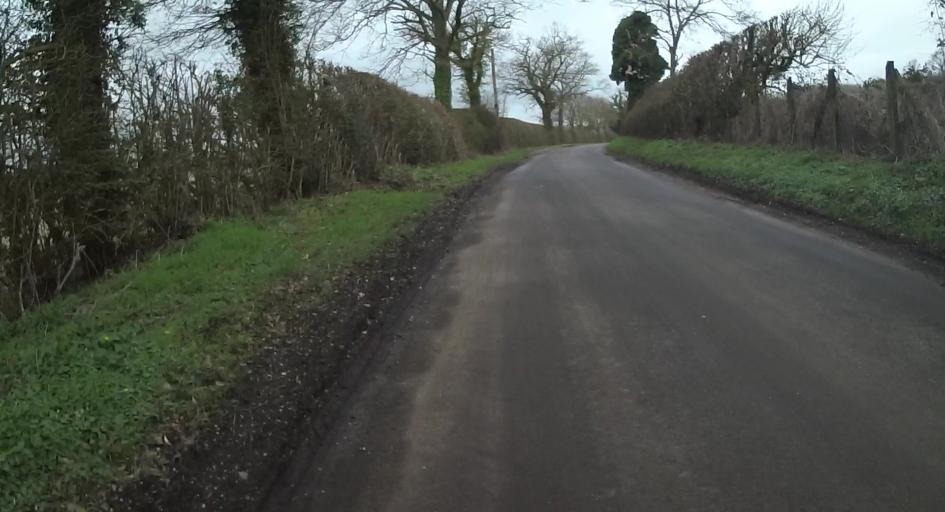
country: GB
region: England
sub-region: Hampshire
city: Overton
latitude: 51.2632
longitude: -1.1965
